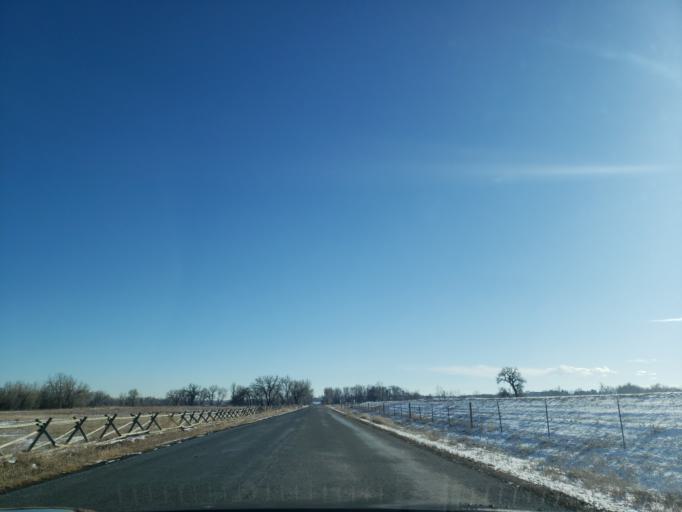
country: US
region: Colorado
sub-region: Larimer County
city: Fort Collins
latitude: 40.5346
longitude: -105.0013
